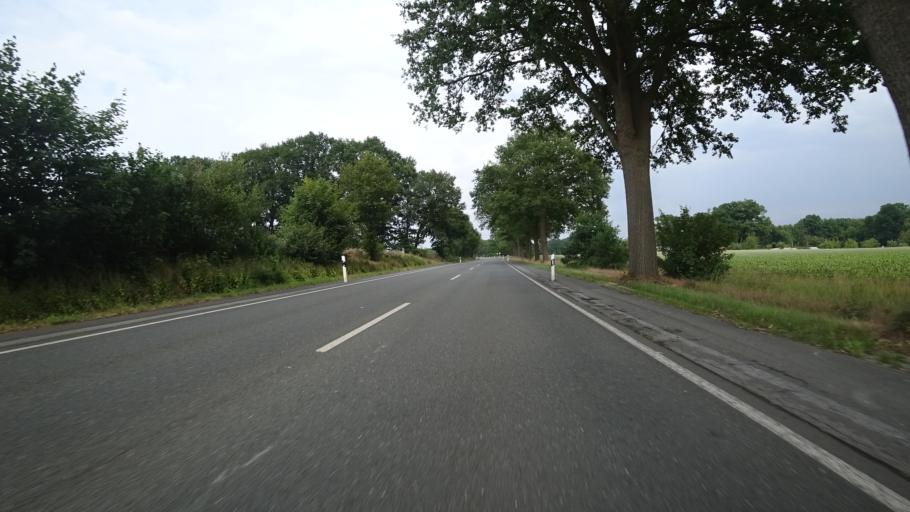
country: DE
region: North Rhine-Westphalia
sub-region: Regierungsbezirk Detmold
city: Guetersloh
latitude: 51.9515
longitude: 8.3578
